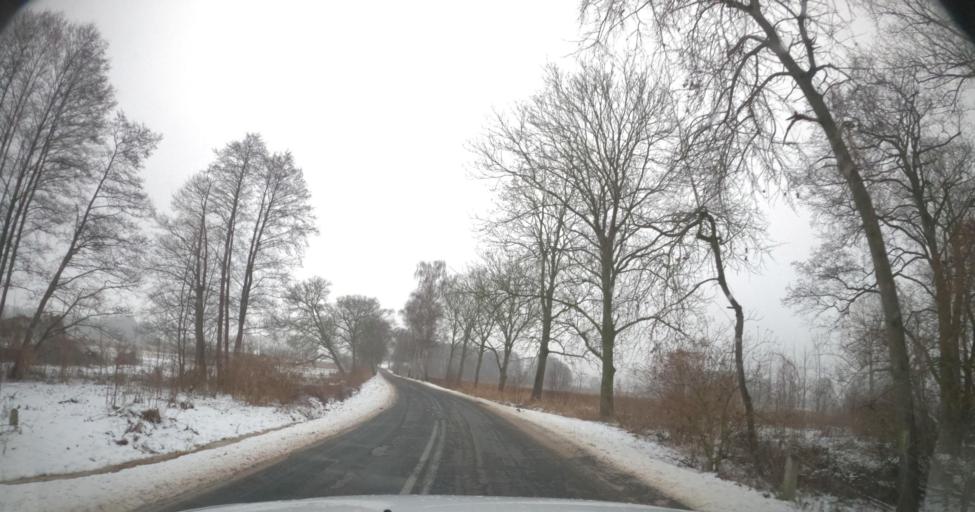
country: PL
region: West Pomeranian Voivodeship
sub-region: Powiat gryficki
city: Brojce
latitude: 53.8997
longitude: 15.2990
